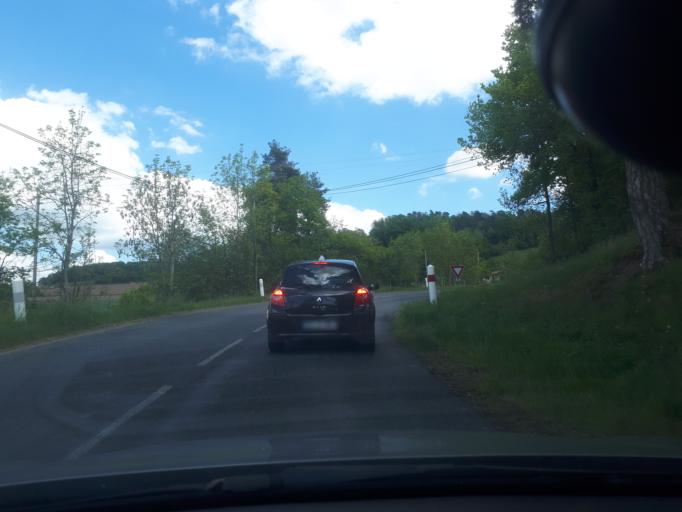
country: FR
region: Rhone-Alpes
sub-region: Departement du Rhone
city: Haute-Rivoire
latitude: 45.7248
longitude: 4.4125
